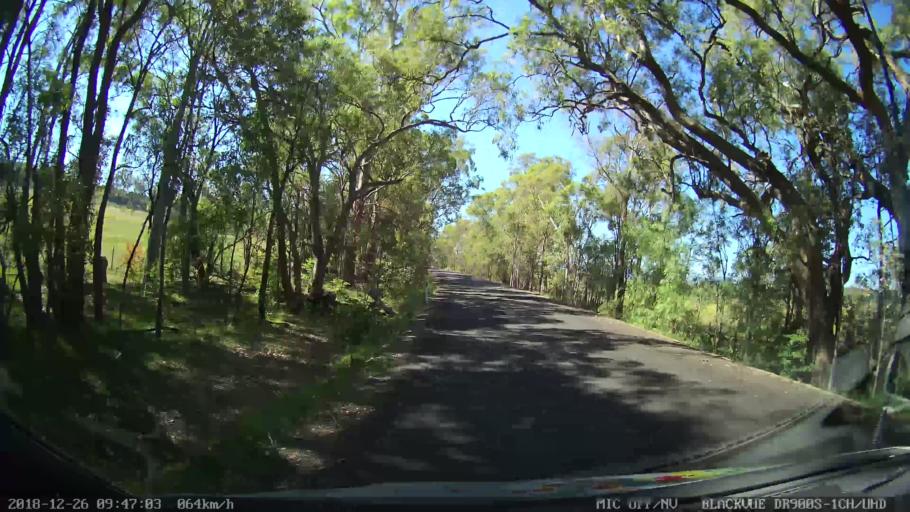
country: AU
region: New South Wales
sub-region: Mid-Western Regional
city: Kandos
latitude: -32.9757
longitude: 150.1043
